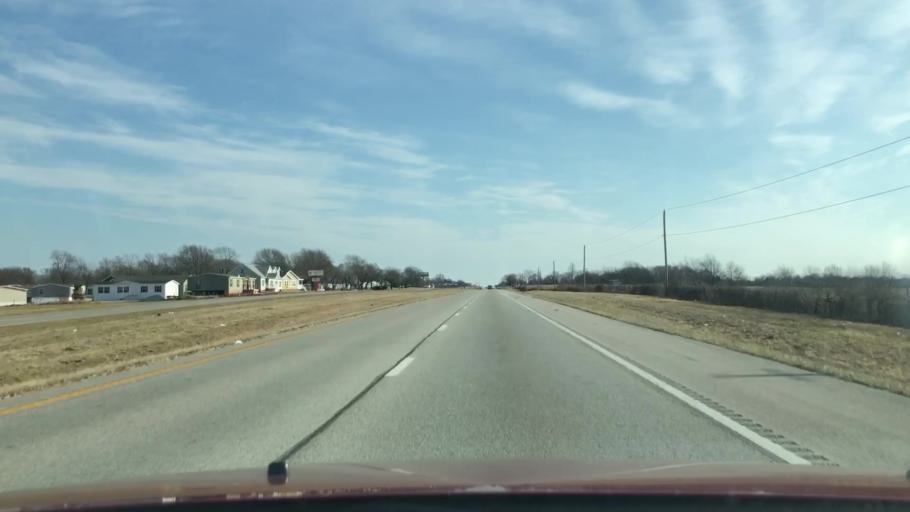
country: US
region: Missouri
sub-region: Webster County
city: Rogersville
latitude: 37.1188
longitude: -93.1345
